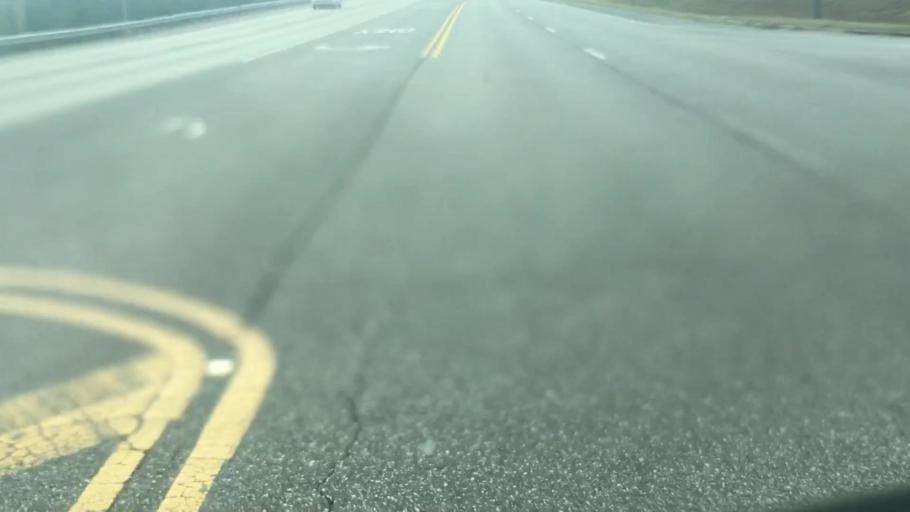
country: US
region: Alabama
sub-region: Walker County
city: Jasper
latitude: 33.8173
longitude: -87.2334
